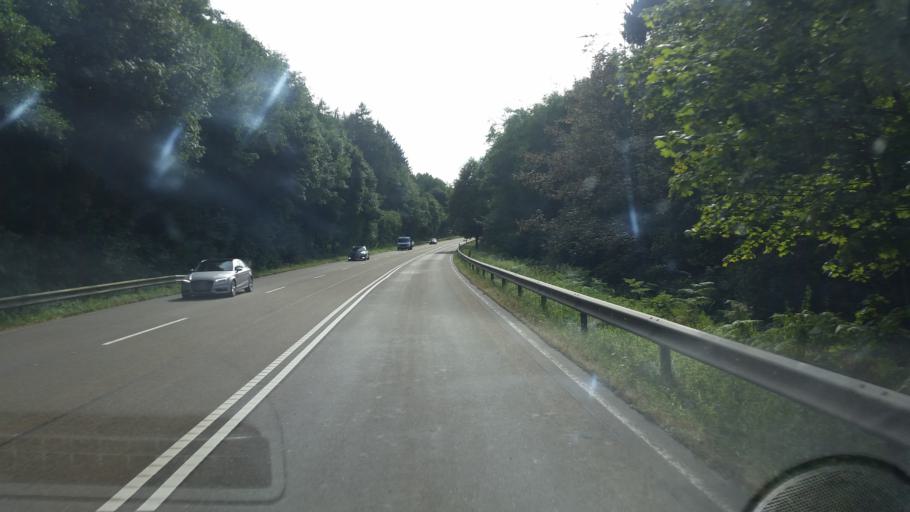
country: DE
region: Rheinland-Pfalz
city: Fachbach
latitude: 50.3526
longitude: 7.6781
